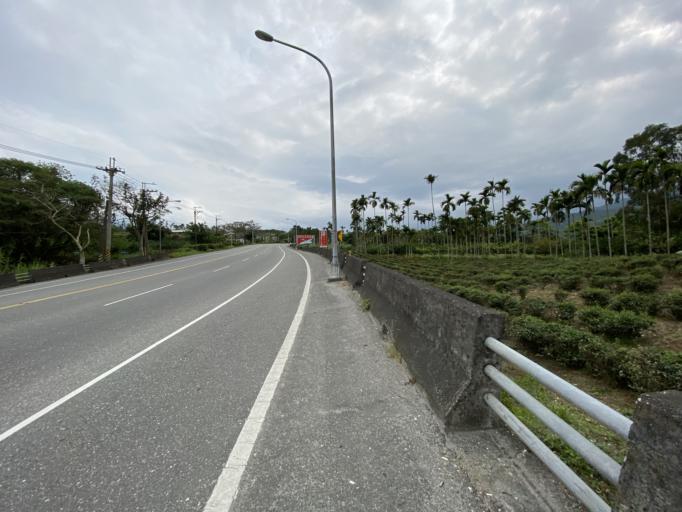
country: TW
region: Taiwan
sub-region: Hualien
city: Hualian
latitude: 23.4705
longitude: 121.3599
